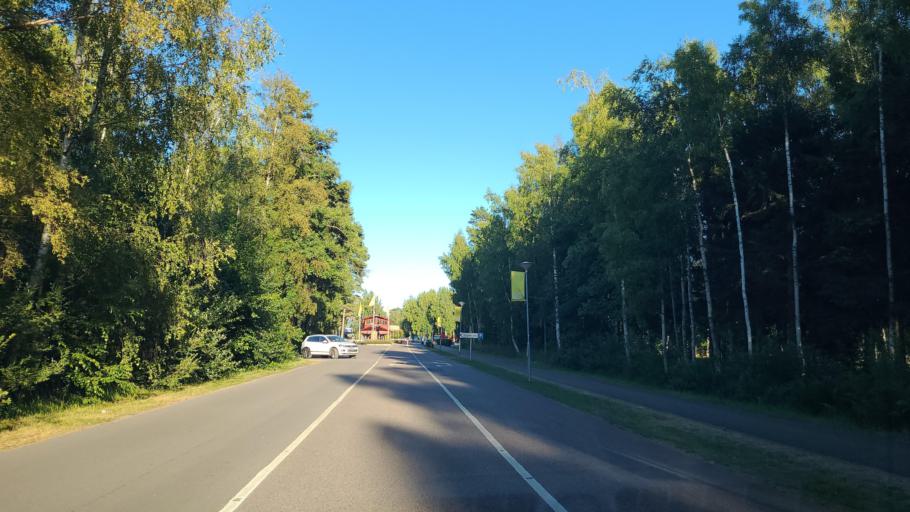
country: SE
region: Kalmar
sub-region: Borgholms Kommun
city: Borgholm
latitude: 57.2749
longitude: 17.0461
